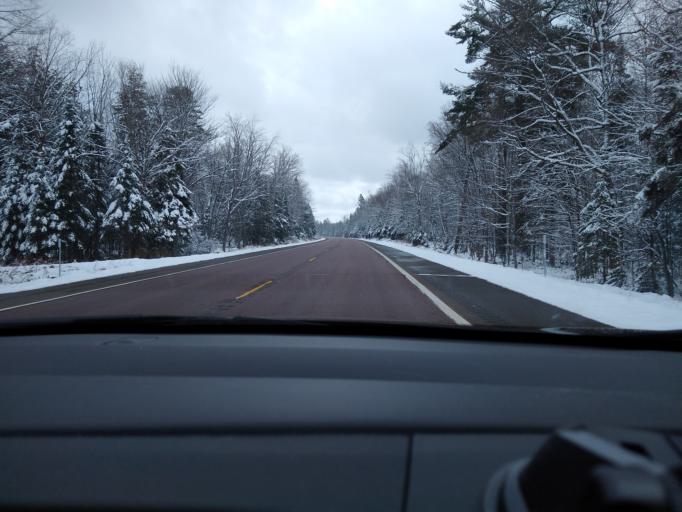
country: US
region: Michigan
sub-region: Iron County
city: Iron River
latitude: 46.1725
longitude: -88.9420
